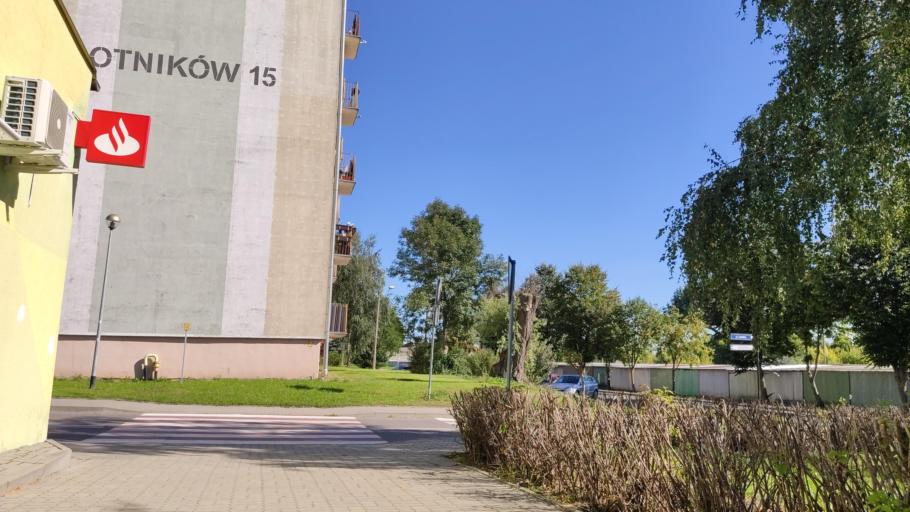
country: PL
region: Kujawsko-Pomorskie
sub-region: Powiat zninski
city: Barcin
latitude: 52.8534
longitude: 17.9415
